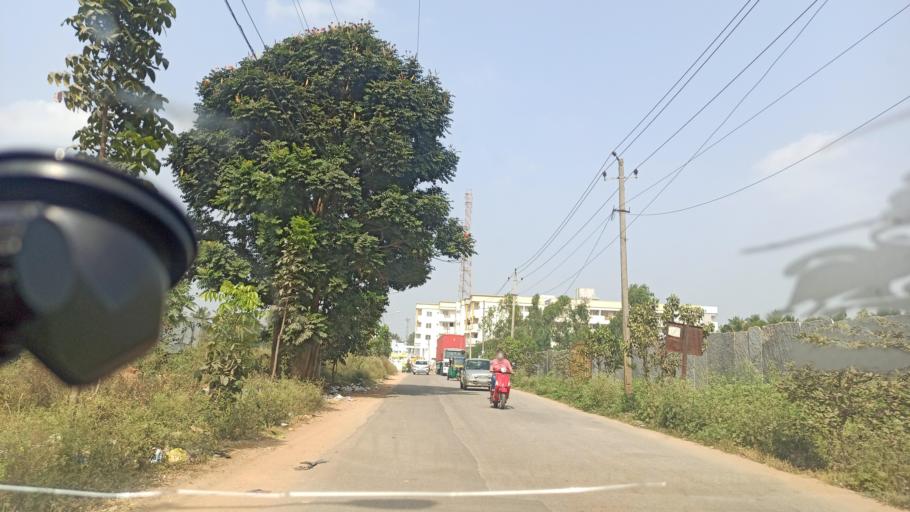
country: IN
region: Karnataka
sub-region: Bangalore Urban
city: Yelahanka
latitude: 13.1008
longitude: 77.6171
